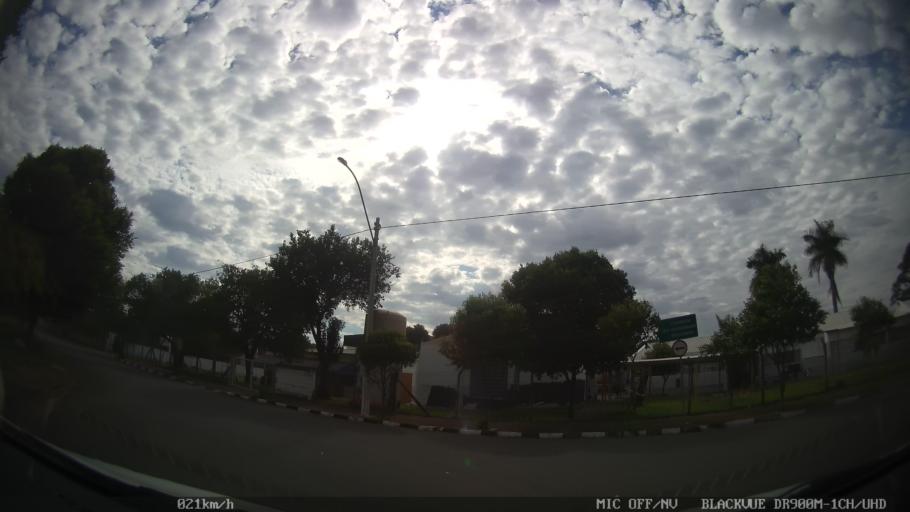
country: BR
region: Sao Paulo
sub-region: Americana
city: Americana
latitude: -22.7211
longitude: -47.3627
